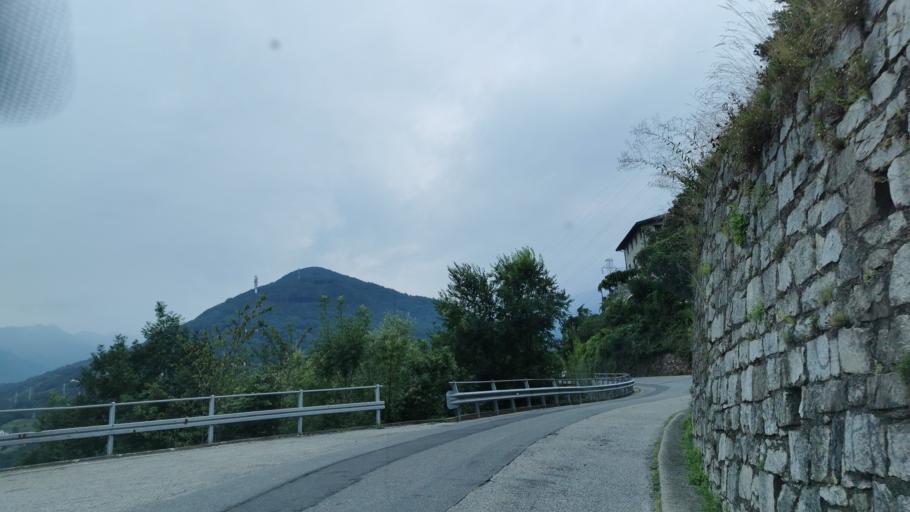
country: IT
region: Lombardy
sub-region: Provincia di Como
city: Gravedona-San Gregorio
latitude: 46.1518
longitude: 9.3042
